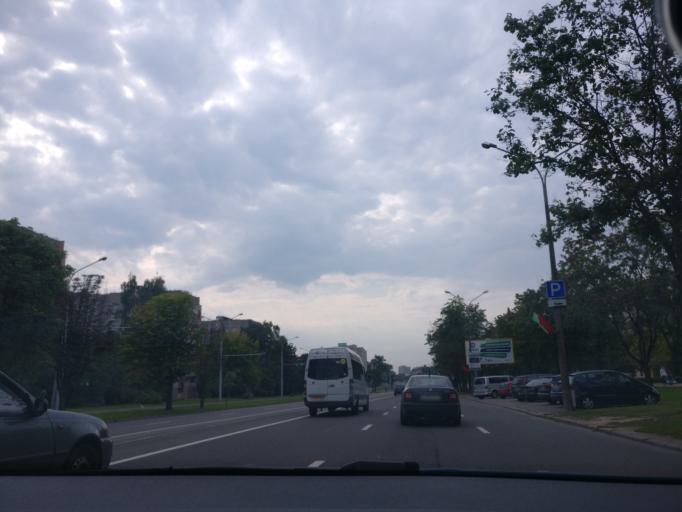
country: BY
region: Minsk
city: Minsk
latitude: 53.9410
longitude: 27.6073
